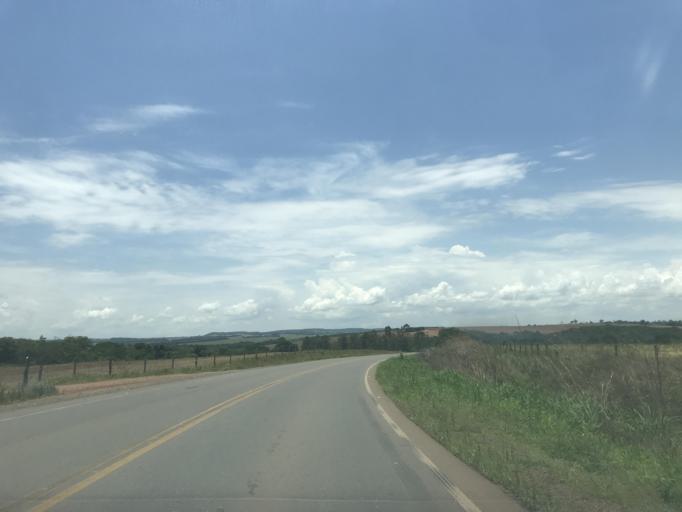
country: BR
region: Goias
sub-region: Vianopolis
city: Vianopolis
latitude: -16.6352
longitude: -48.3559
